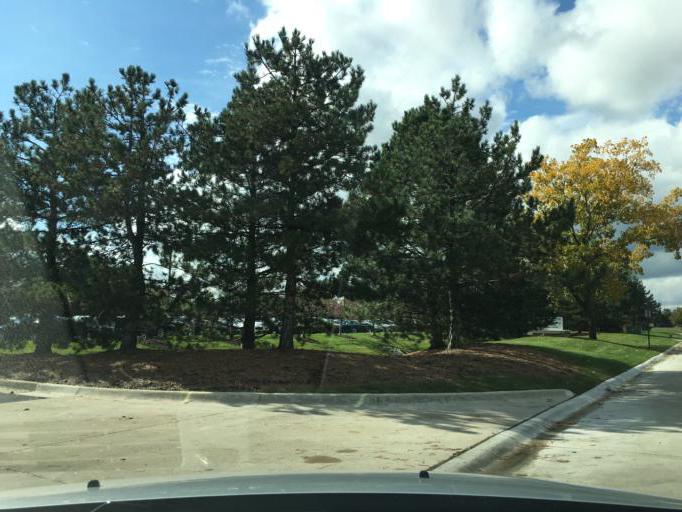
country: US
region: Michigan
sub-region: Wayne County
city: Melvindale
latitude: 42.2949
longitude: -83.2012
